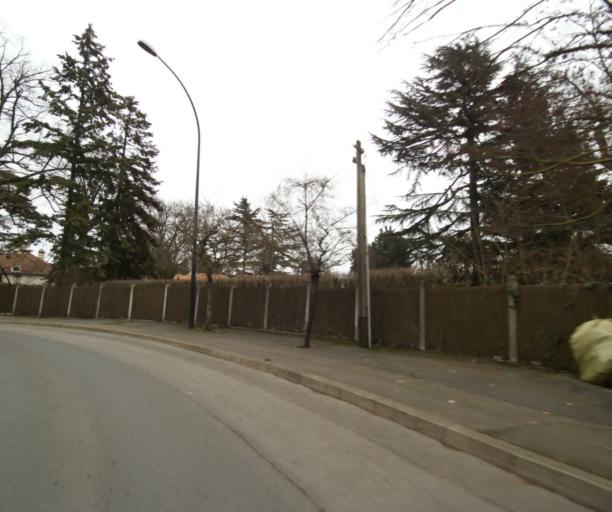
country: FR
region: Ile-de-France
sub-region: Departement des Hauts-de-Seine
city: Garches
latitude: 48.8503
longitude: 2.1874
